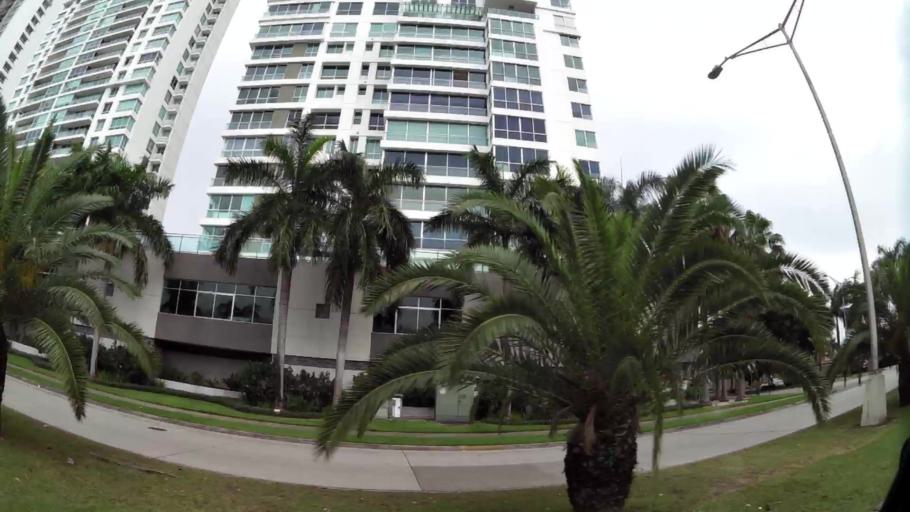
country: PA
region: Panama
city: San Miguelito
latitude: 9.0105
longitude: -79.4617
